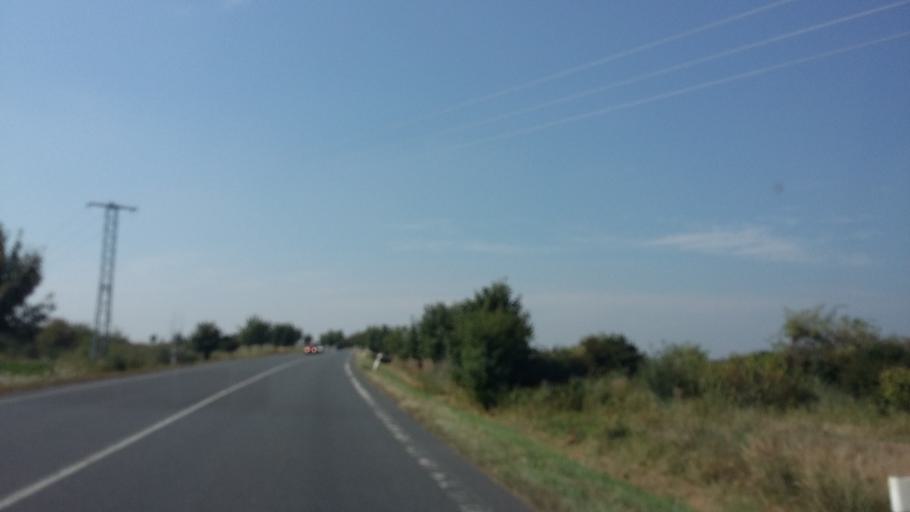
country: CZ
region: Central Bohemia
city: Velky Osek
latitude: 50.0951
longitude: 15.2601
